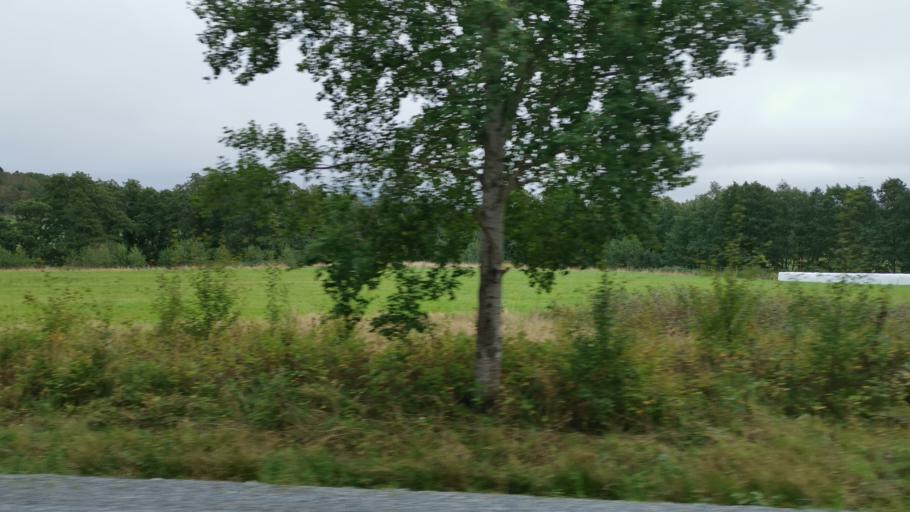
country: SE
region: Vaestra Goetaland
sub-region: Tanums Kommun
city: Tanumshede
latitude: 58.6981
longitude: 11.3385
